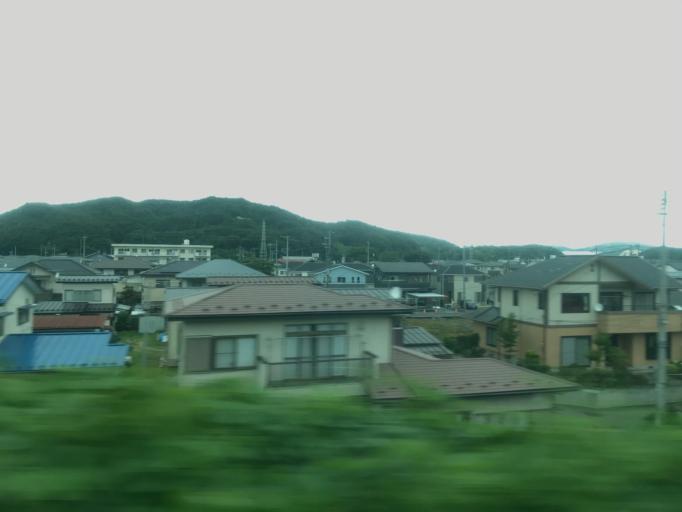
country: JP
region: Tochigi
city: Kuroiso
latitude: 37.1320
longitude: 140.2042
